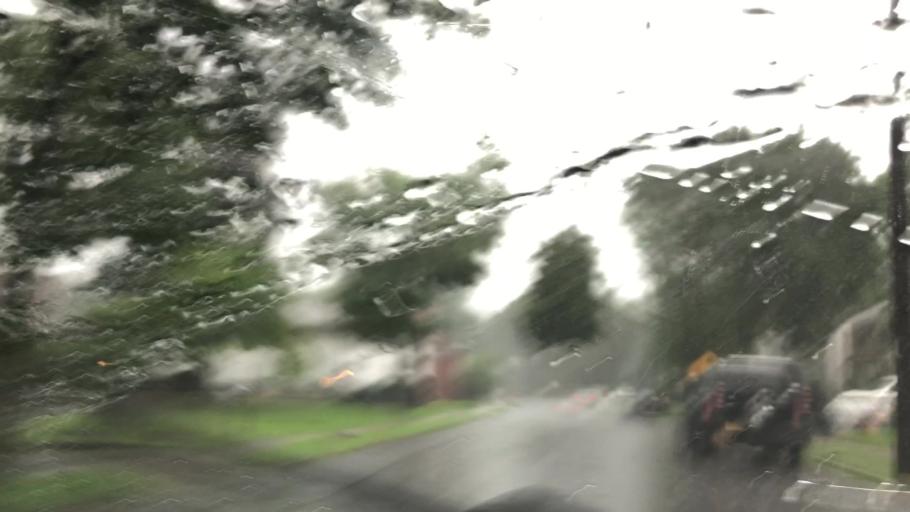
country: US
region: New Jersey
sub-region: Bergen County
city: Elmwood Park
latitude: 40.9159
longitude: -74.1154
